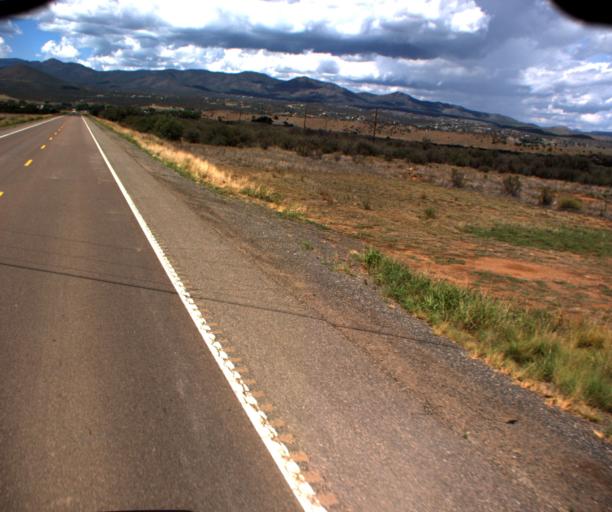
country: US
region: Arizona
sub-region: Yavapai County
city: Dewey-Humboldt
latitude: 34.5357
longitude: -112.2116
